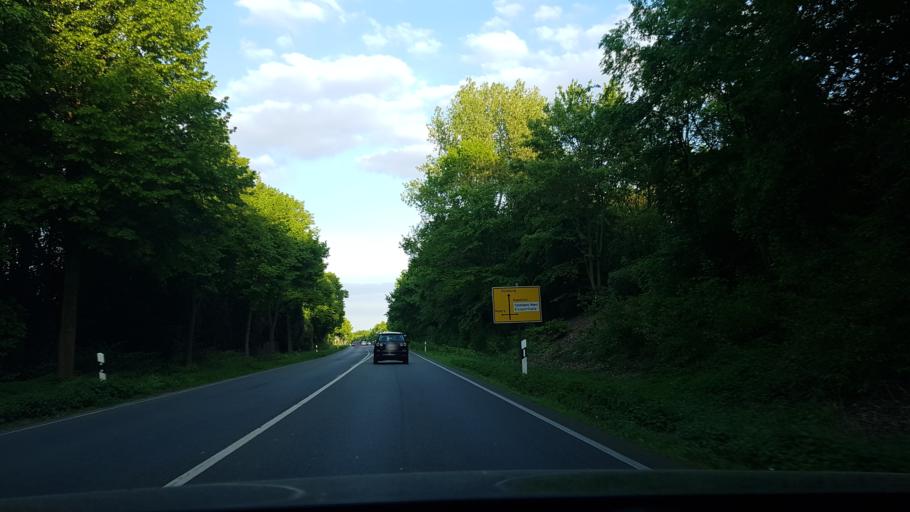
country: DE
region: North Rhine-Westphalia
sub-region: Regierungsbezirk Dusseldorf
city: Moers
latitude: 51.4413
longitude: 6.6174
